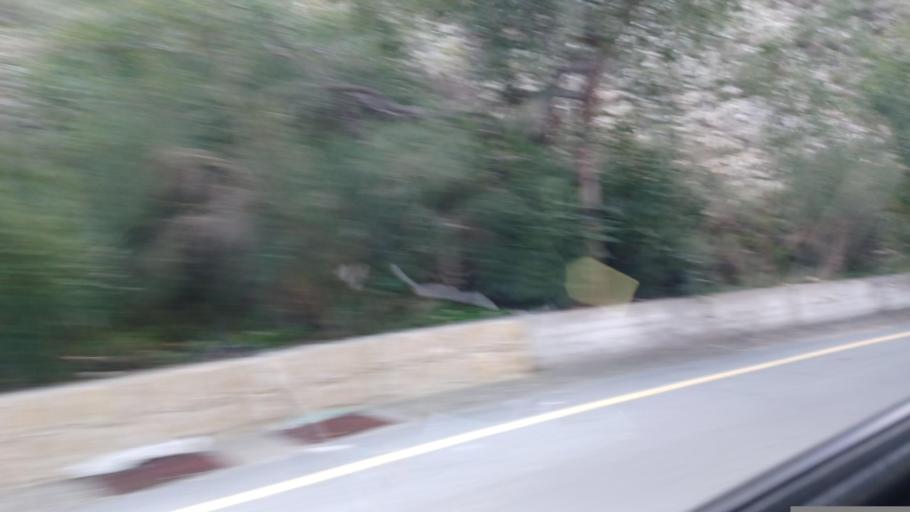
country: CY
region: Limassol
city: Pachna
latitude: 34.8373
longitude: 32.7924
